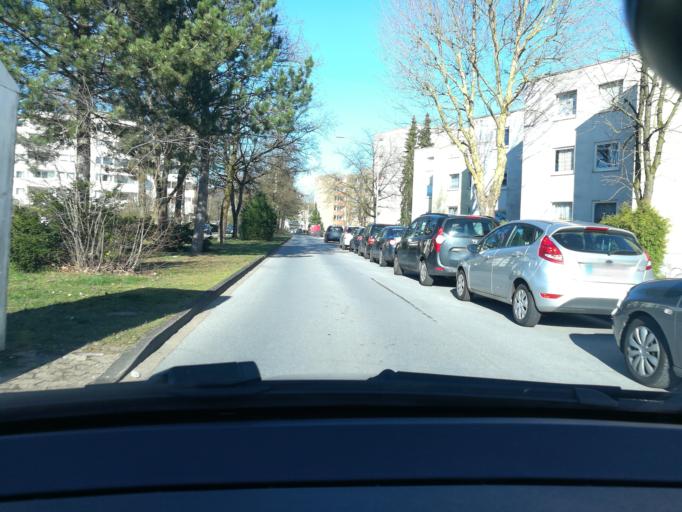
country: DE
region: North Rhine-Westphalia
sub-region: Regierungsbezirk Detmold
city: Oerlinghausen
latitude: 51.9516
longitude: 8.6047
